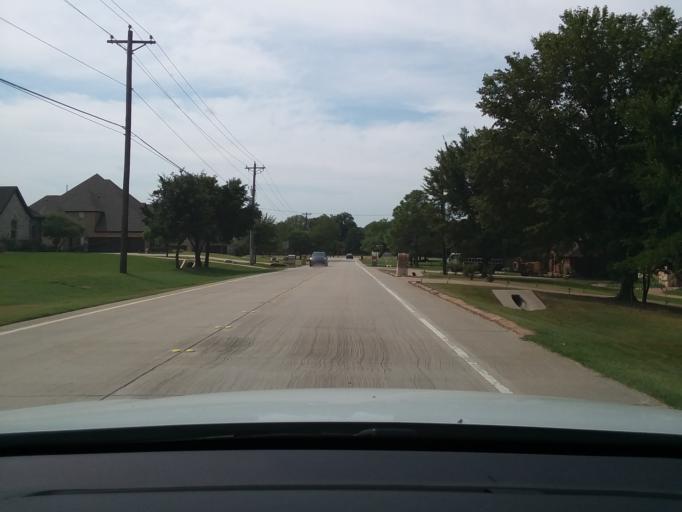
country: US
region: Texas
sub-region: Denton County
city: Double Oak
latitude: 33.0600
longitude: -97.1143
